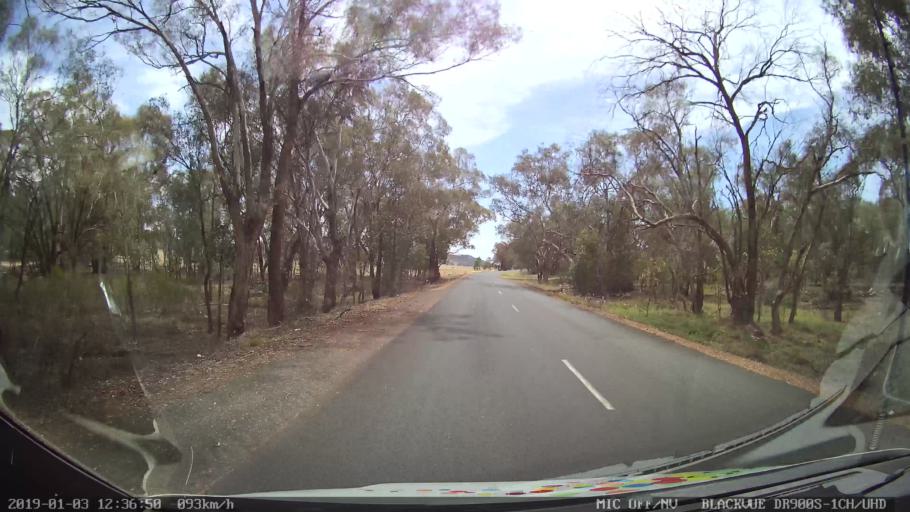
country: AU
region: New South Wales
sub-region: Weddin
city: Grenfell
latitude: -33.8497
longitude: 148.1789
